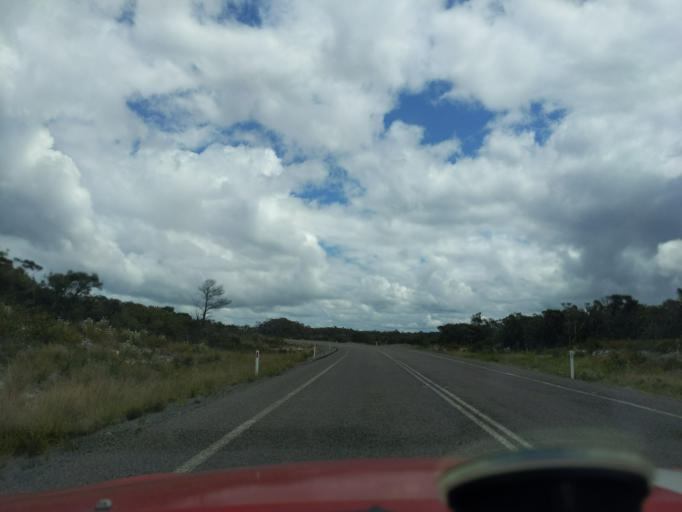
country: AU
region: New South Wales
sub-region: Great Lakes
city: Hawks Nest
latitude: -32.5958
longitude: 152.2502
